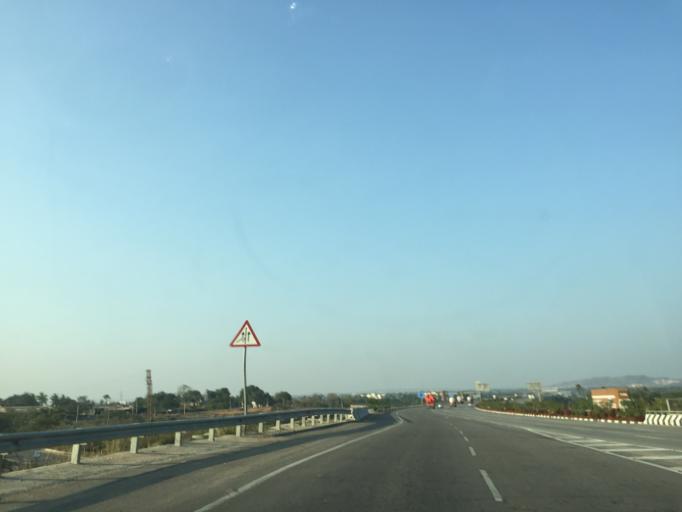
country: IN
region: Telangana
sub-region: Rangareddi
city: Ghatkesar
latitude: 17.4451
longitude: 78.6678
